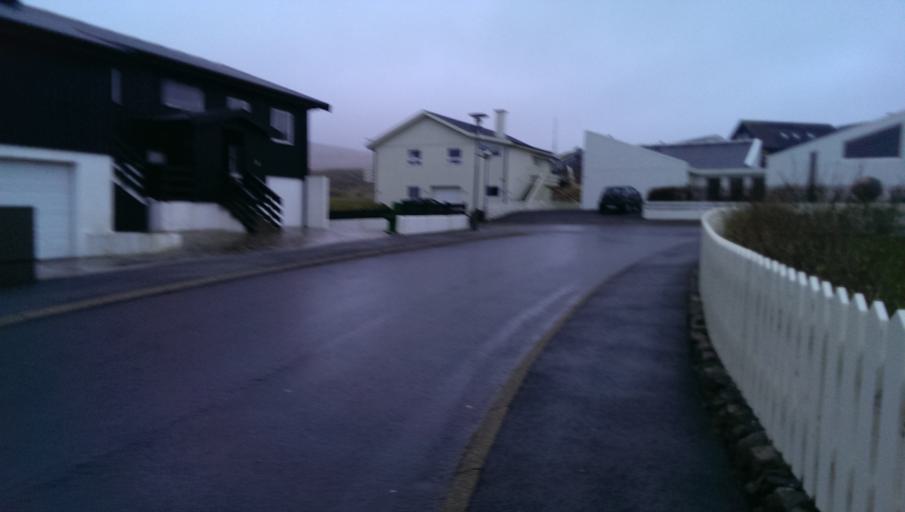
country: FO
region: Streymoy
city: Hoyvik
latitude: 62.0324
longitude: -6.7886
